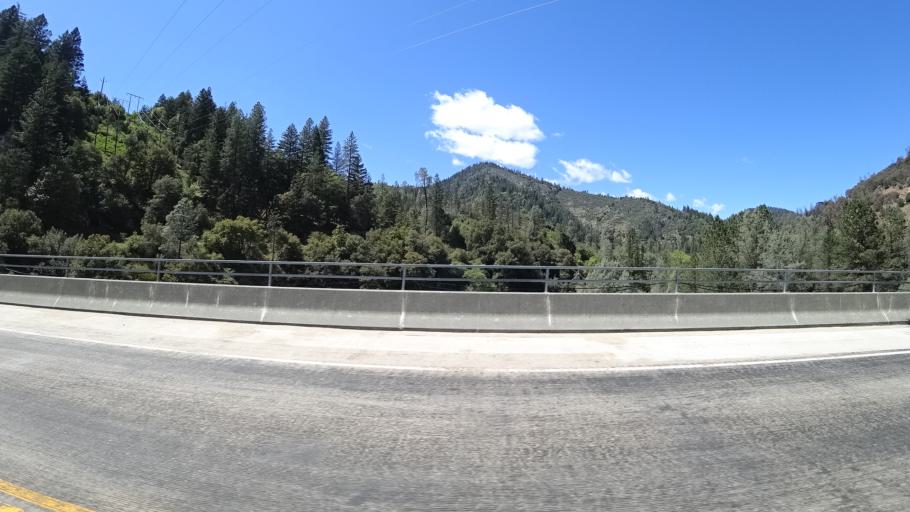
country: US
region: California
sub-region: Trinity County
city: Weaverville
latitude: 40.7704
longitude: -123.1277
